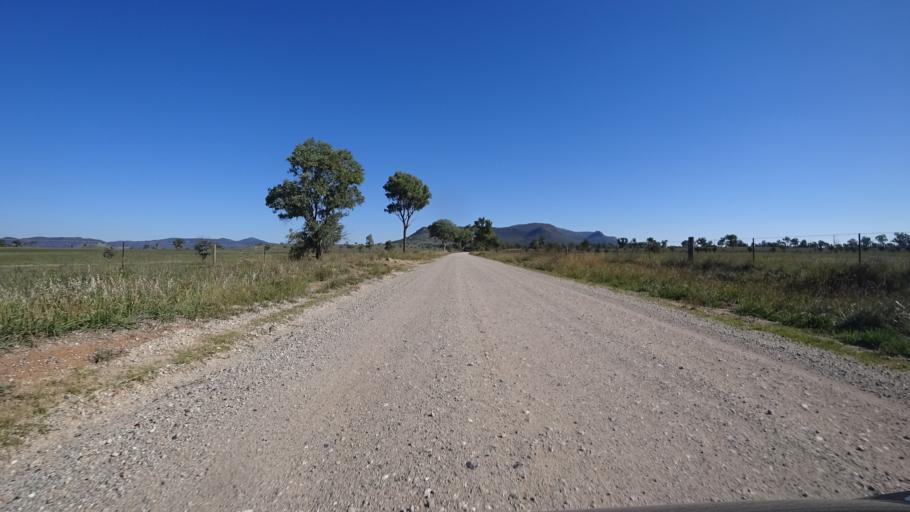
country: AU
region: New South Wales
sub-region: Mid-Western Regional
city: Kandos
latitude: -32.8197
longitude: 150.0226
